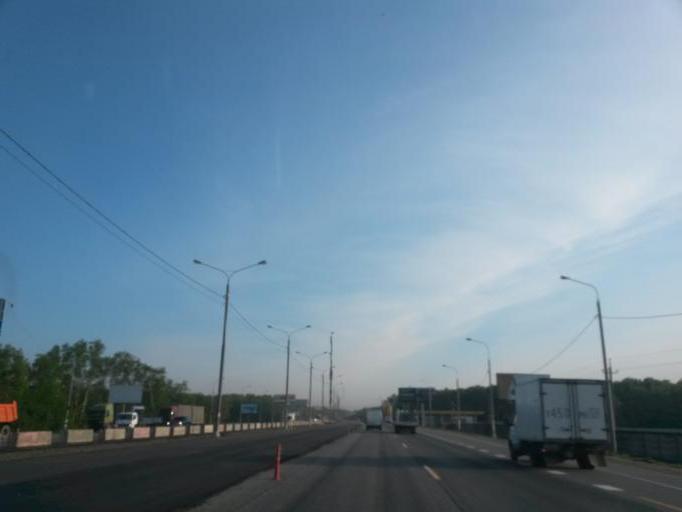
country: RU
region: Moscow
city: Annino
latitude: 55.5364
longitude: 37.6105
